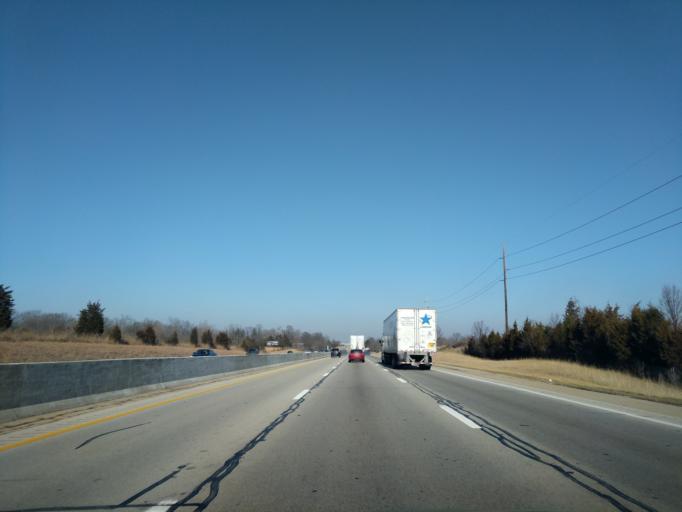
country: US
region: Ohio
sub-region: Montgomery County
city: Vandalia
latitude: 39.9253
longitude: -84.1885
